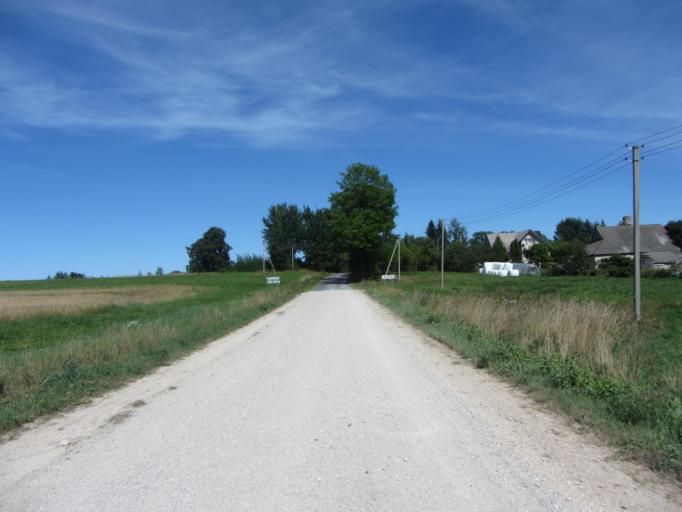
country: LT
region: Utenos apskritis
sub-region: Utena
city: Utena
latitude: 55.6974
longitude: 25.5173
